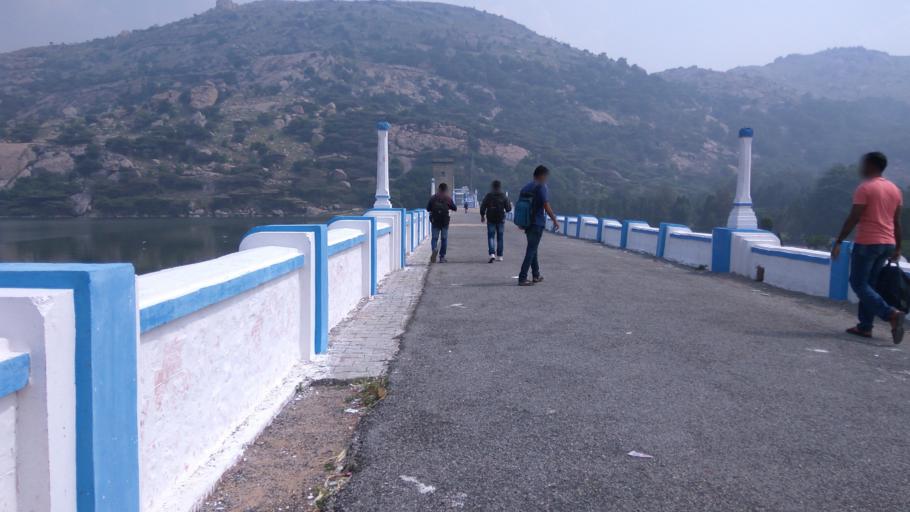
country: IN
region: Tamil Nadu
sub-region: Krishnagiri
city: Krishnagiri
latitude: 12.4762
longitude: 78.1860
